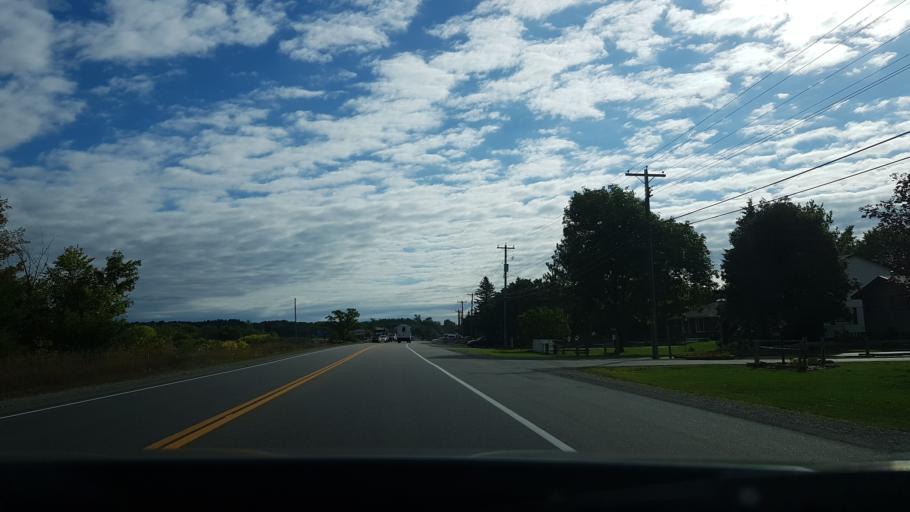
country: CA
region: Ontario
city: Orillia
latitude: 44.6150
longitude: -79.4954
